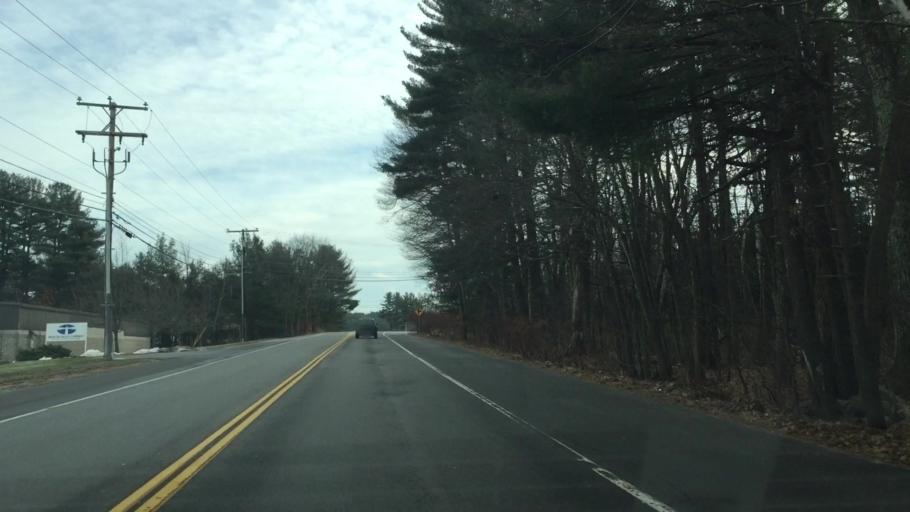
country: US
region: New Hampshire
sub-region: Hillsborough County
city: Manchester
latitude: 42.9386
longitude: -71.4203
